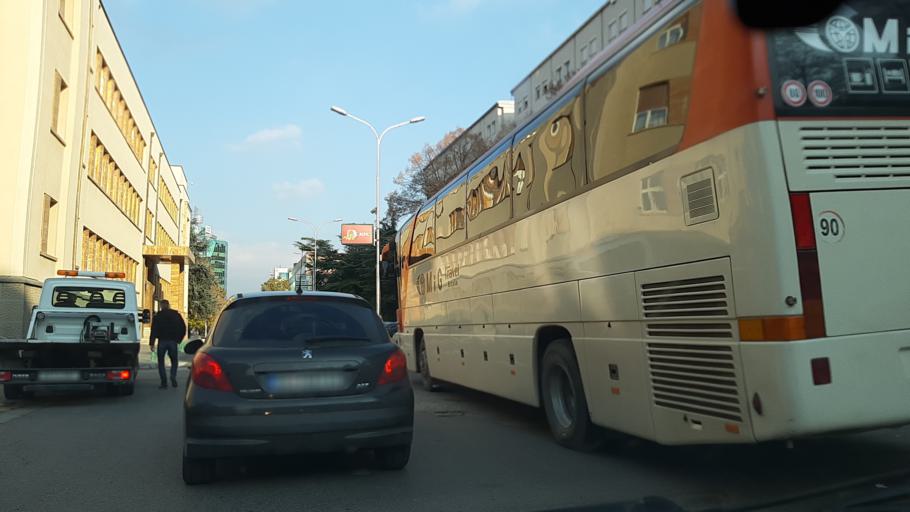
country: MK
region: Karpos
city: Skopje
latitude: 41.9921
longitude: 21.4322
